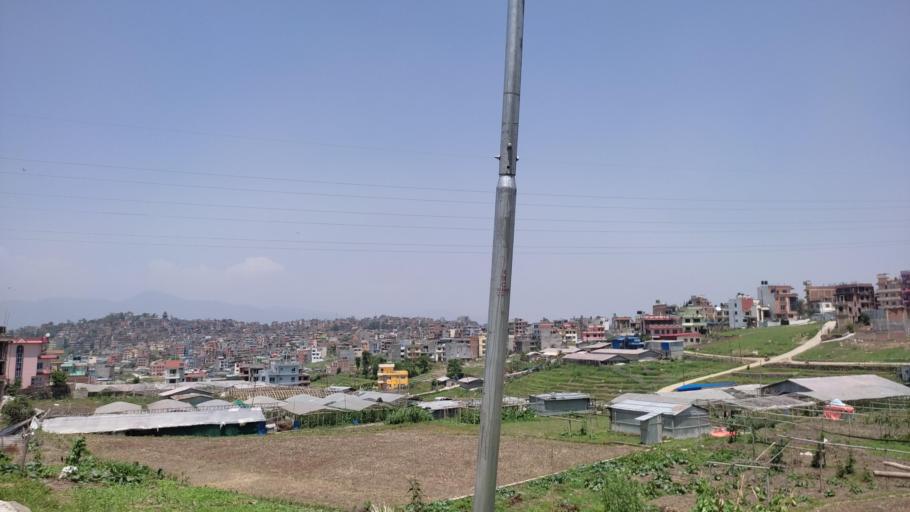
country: NP
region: Central Region
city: Kirtipur
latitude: 27.6694
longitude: 85.2654
